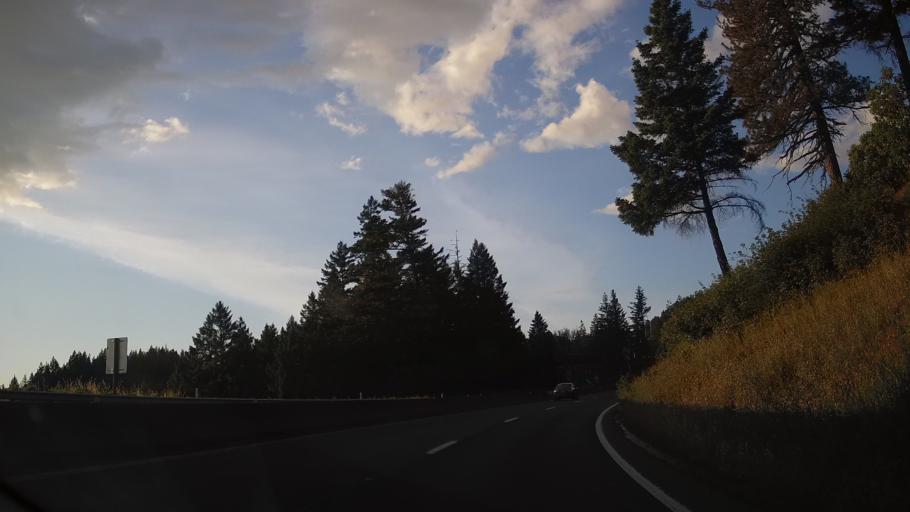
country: US
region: California
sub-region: Mendocino County
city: Willits
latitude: 39.3316
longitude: -123.3046
